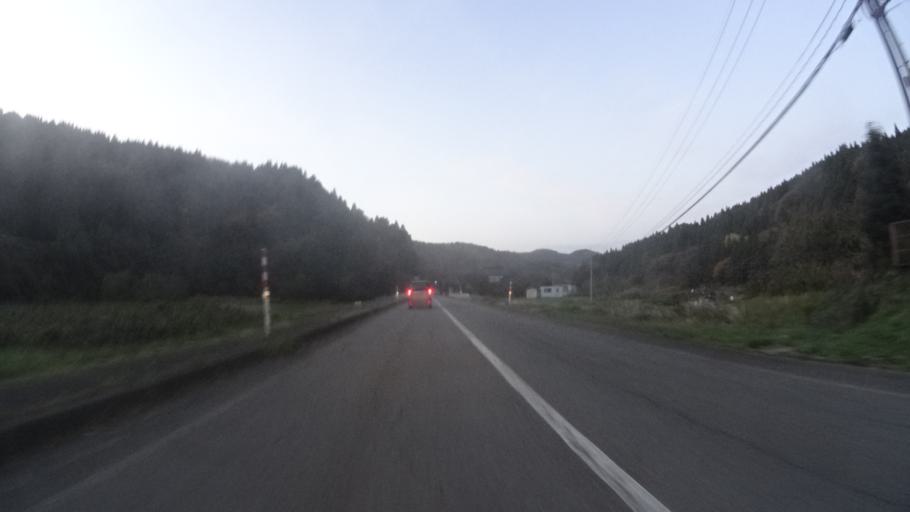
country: JP
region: Ishikawa
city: Nanao
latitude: 37.3570
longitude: 136.8669
